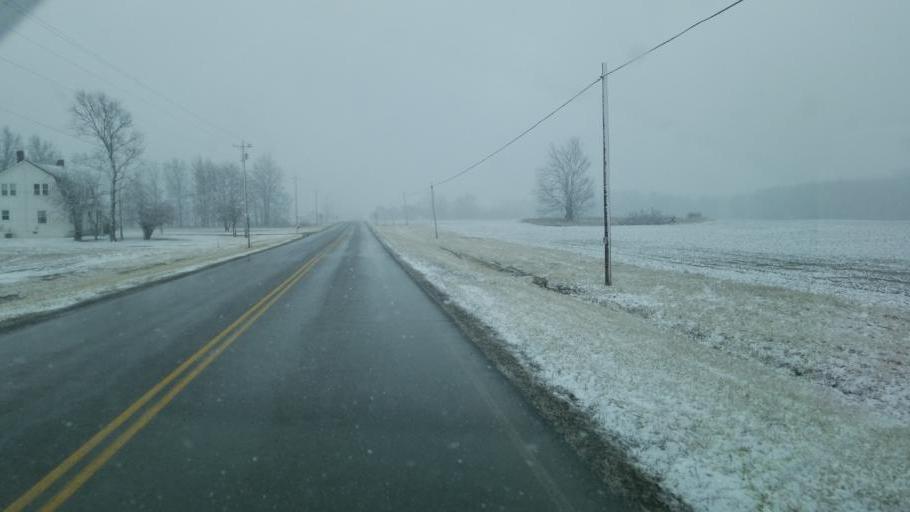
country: US
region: Ohio
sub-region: Champaign County
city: North Lewisburg
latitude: 40.3399
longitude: -83.5412
